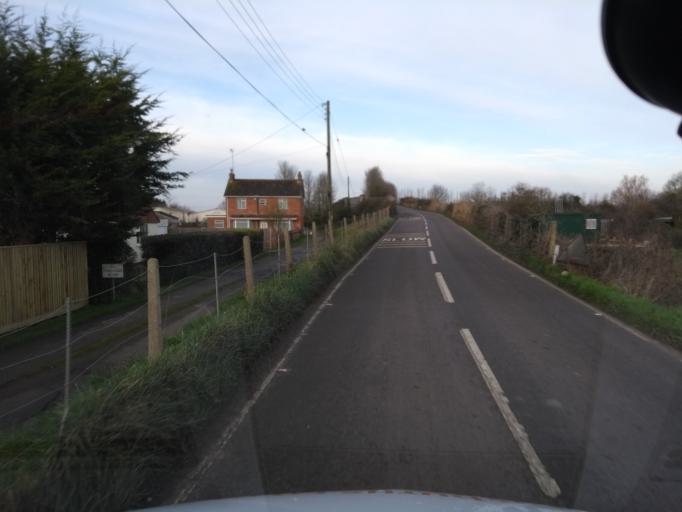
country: GB
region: England
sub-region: Somerset
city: Burnham-on-Sea
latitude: 51.2583
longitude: -2.9689
